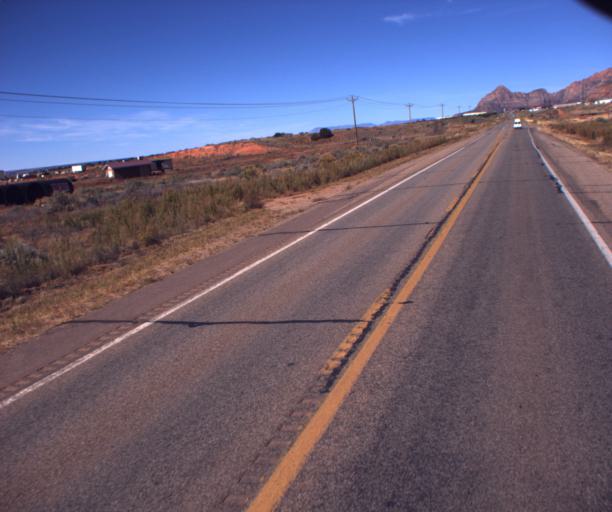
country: US
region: Arizona
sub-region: Mohave County
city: Colorado City
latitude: 36.9890
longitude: -112.9898
